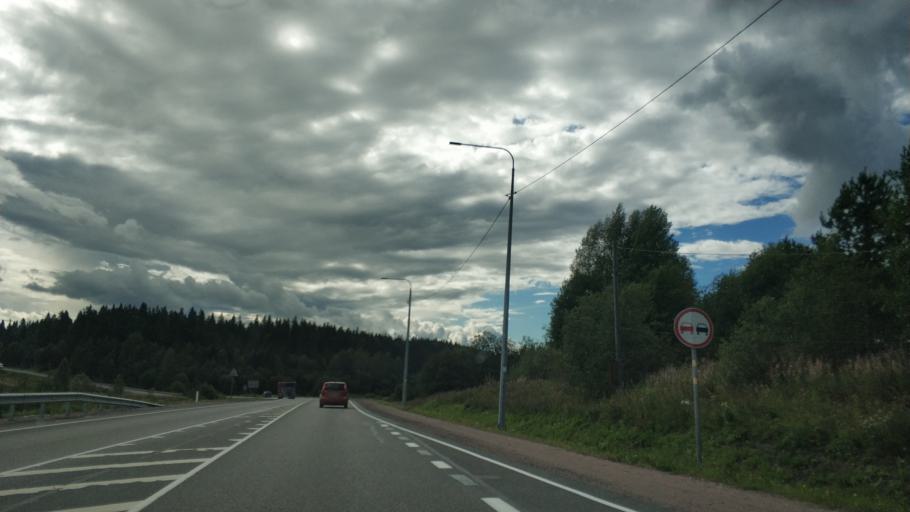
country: RU
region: Republic of Karelia
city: Khelyulya
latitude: 61.7747
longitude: 30.6587
